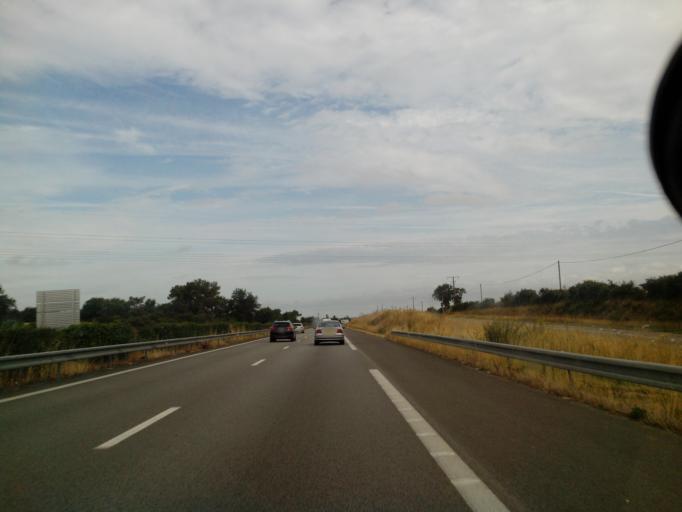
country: FR
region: Brittany
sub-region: Departement du Morbihan
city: Theix
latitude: 47.6189
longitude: -2.6255
